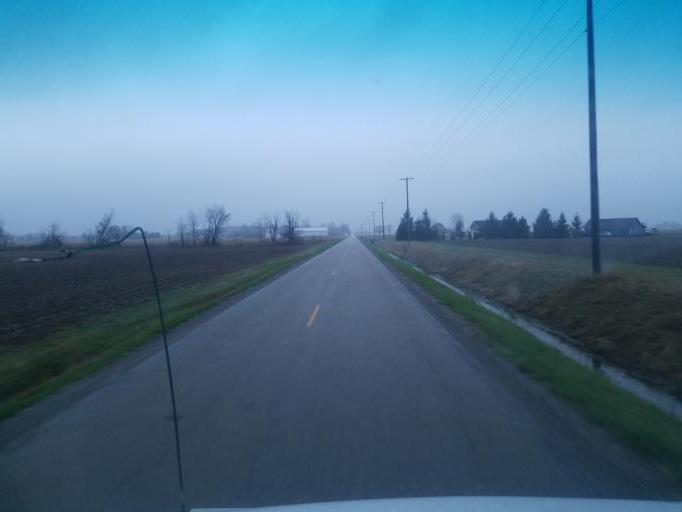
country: US
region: Ohio
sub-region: Fulton County
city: Archbold
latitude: 41.4277
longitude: -84.2782
